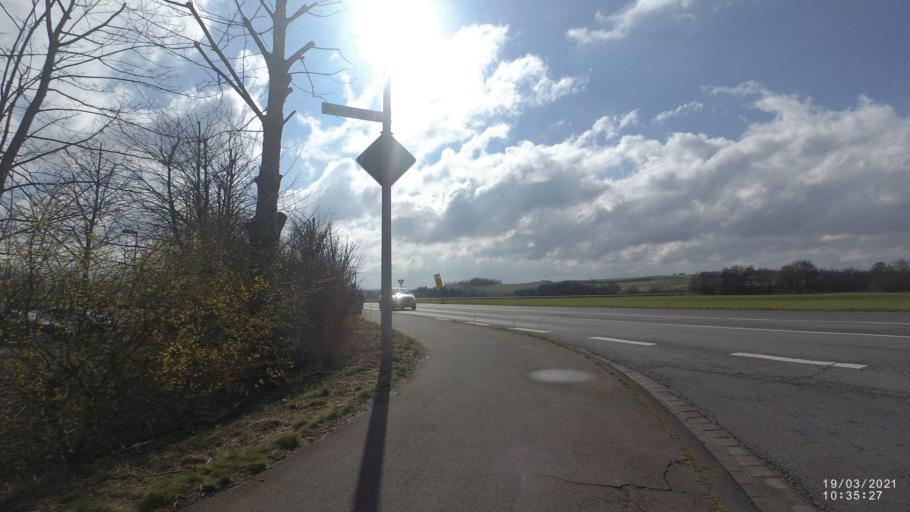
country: DE
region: Rheinland-Pfalz
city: Mendig
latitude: 50.3658
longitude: 7.2946
